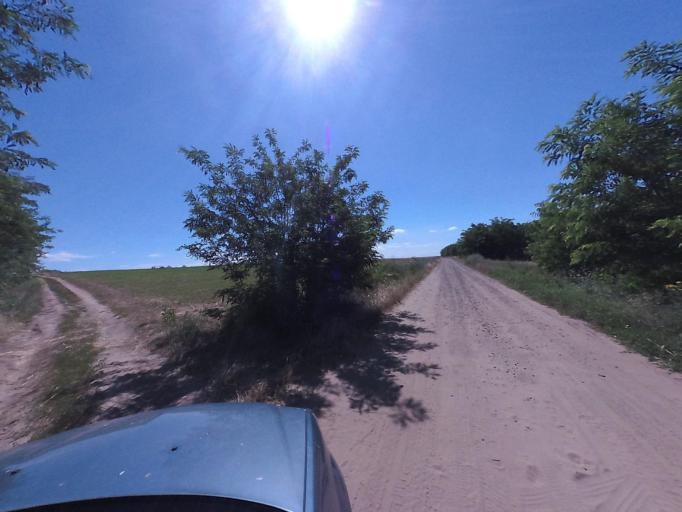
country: RO
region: Vaslui
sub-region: Comuna Costesti
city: Costesti
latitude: 46.4845
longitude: 27.7715
